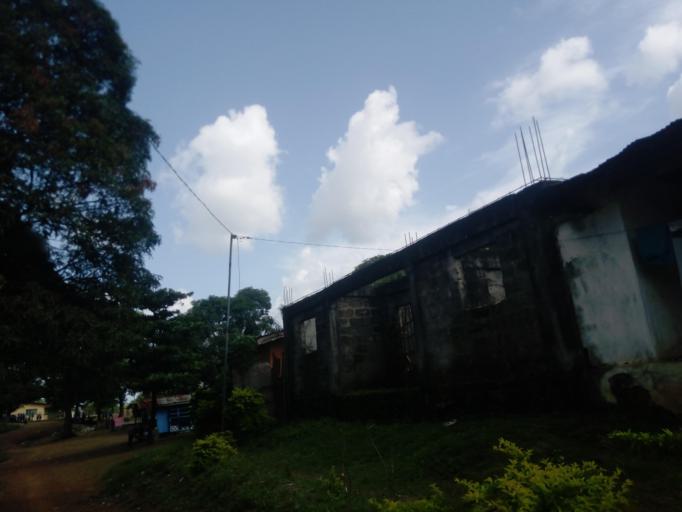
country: SL
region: Northern Province
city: Makeni
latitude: 8.8930
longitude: -12.0323
